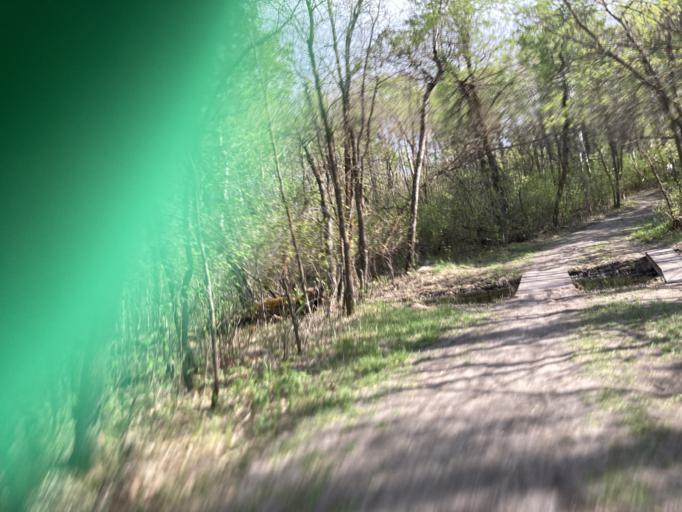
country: CA
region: Manitoba
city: Brandon
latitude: 49.7217
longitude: -99.9075
